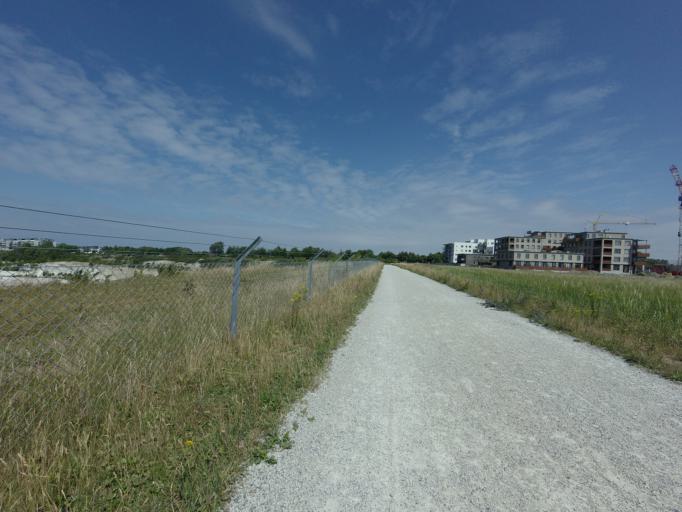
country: SE
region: Skane
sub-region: Malmo
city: Bunkeflostrand
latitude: 55.5677
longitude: 12.9439
